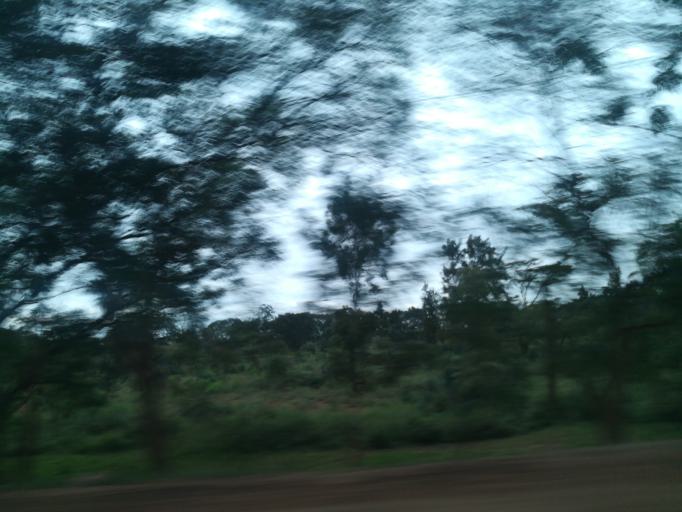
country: KE
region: Nairobi Area
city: Thika
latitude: -1.0376
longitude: 37.0619
